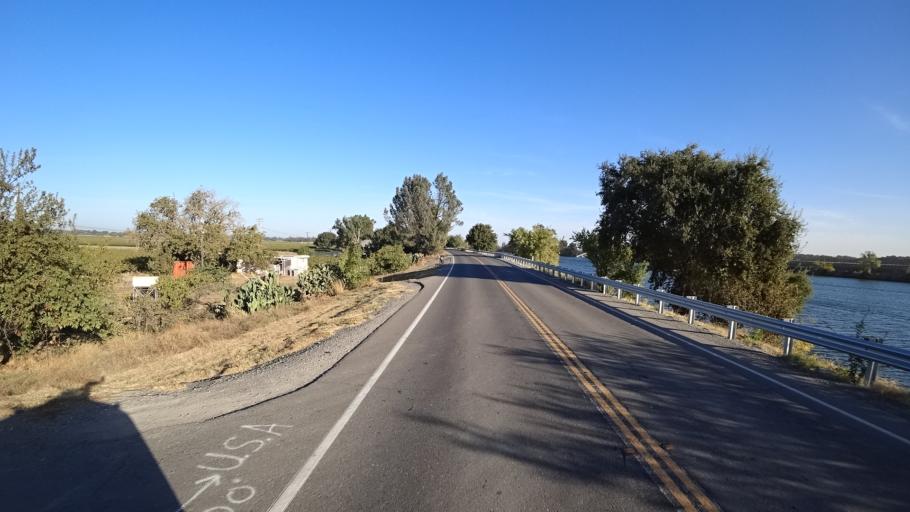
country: US
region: California
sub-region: Sacramento County
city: Laguna
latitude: 38.4001
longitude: -121.5150
